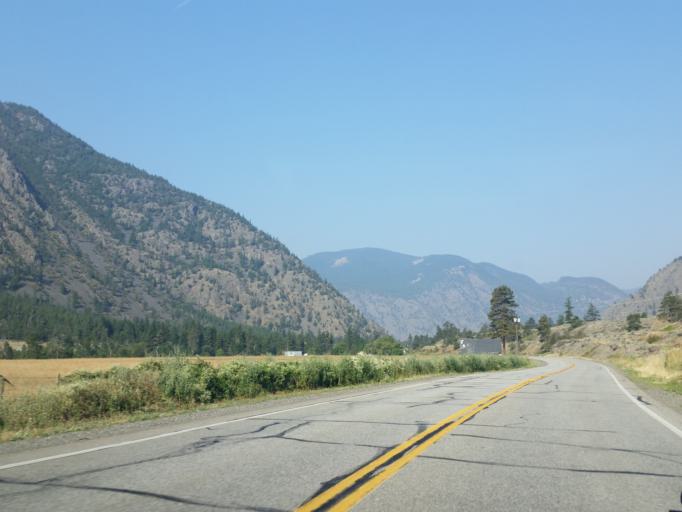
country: CA
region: British Columbia
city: Oliver
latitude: 49.2178
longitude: -119.9194
